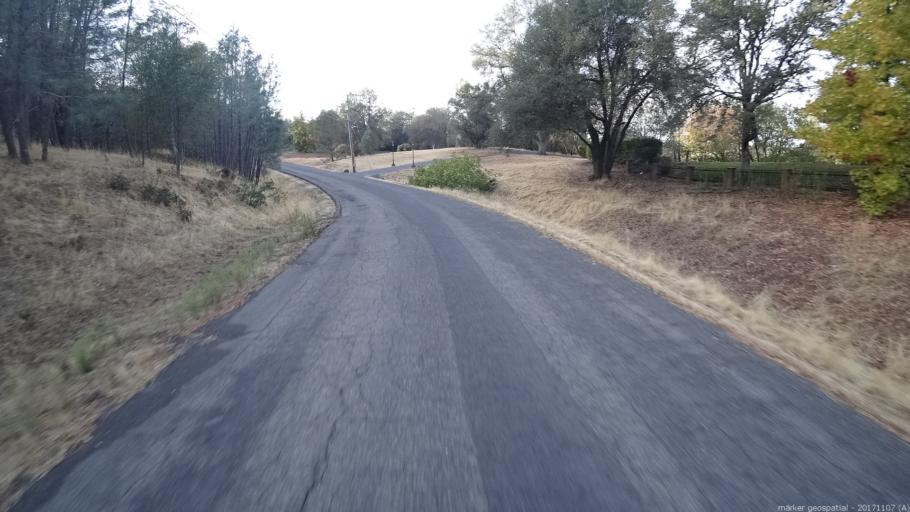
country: US
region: California
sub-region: Shasta County
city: Shasta
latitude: 40.5388
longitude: -122.4823
